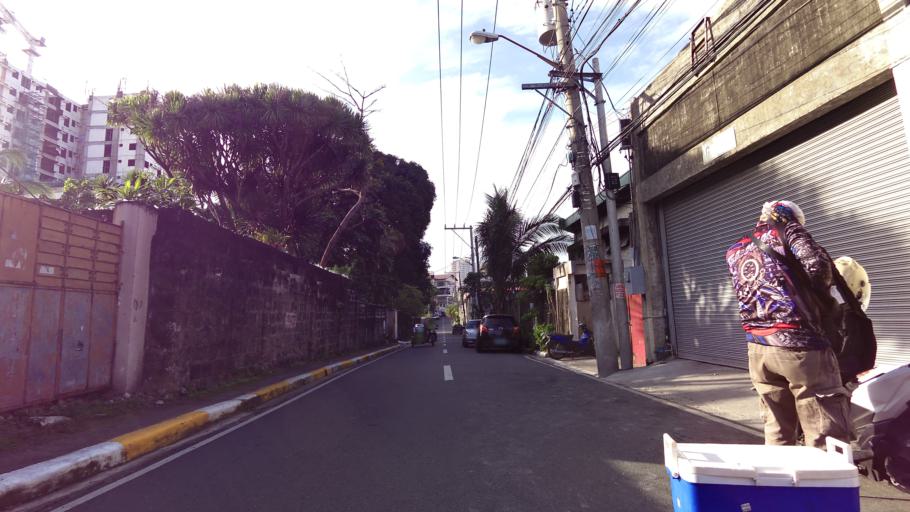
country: PH
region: Metro Manila
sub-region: San Juan
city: San Juan
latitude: 14.6072
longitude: 121.0353
